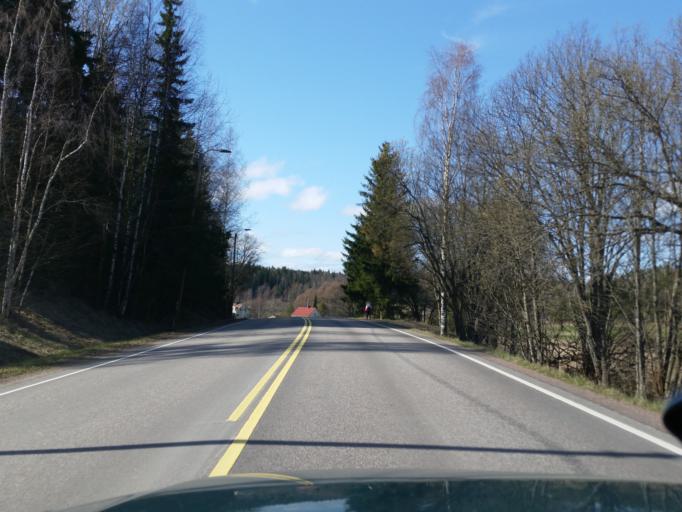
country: FI
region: Uusimaa
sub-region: Helsinki
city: Vihti
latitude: 60.4199
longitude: 24.3200
